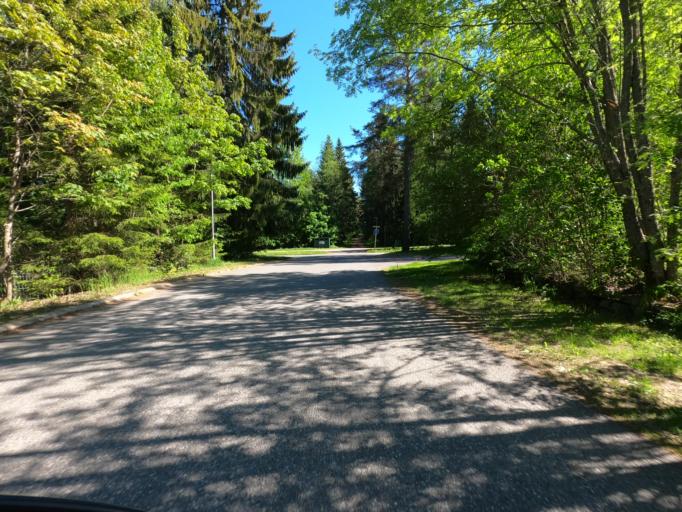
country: FI
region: North Karelia
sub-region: Joensuu
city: Joensuu
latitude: 62.5913
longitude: 29.7985
